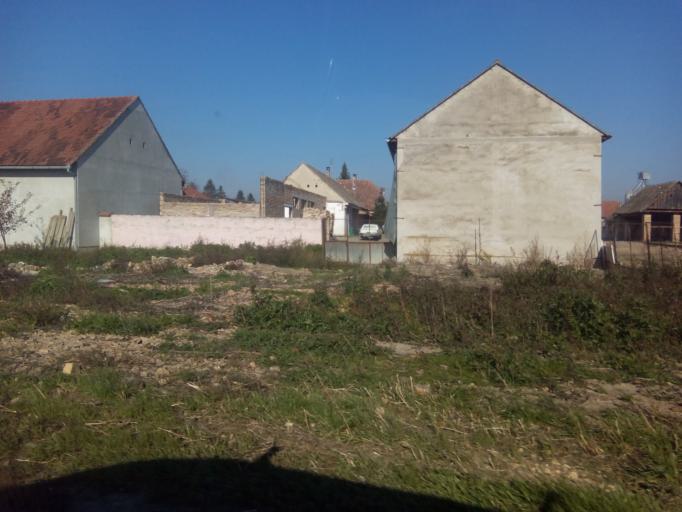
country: RS
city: Glozan
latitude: 45.2743
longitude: 19.5726
